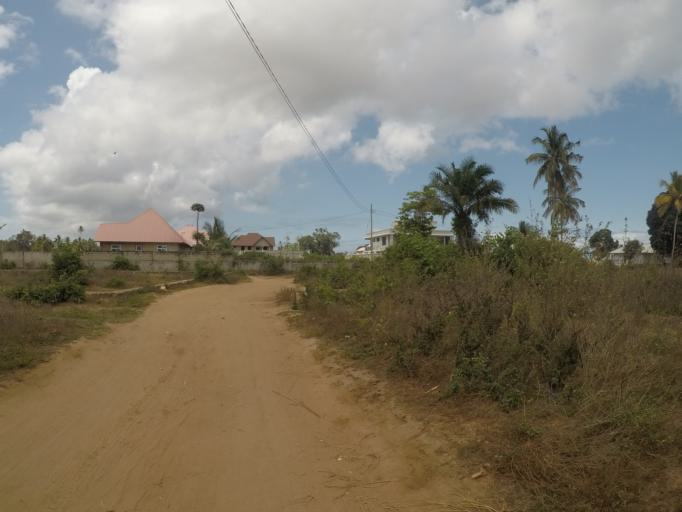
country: TZ
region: Zanzibar Urban/West
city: Zanzibar
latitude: -6.2025
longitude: 39.2320
